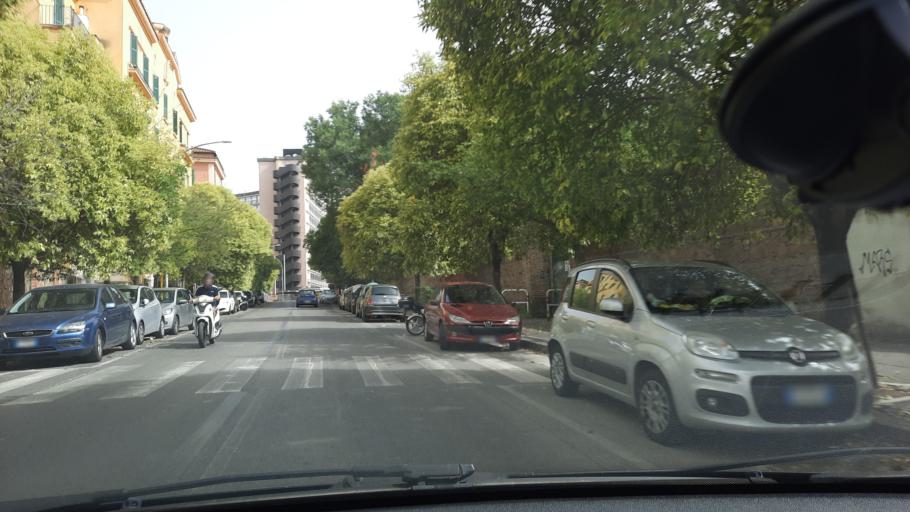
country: IT
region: Latium
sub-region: Citta metropolitana di Roma Capitale
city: Rome
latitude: 41.8611
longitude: 12.4936
